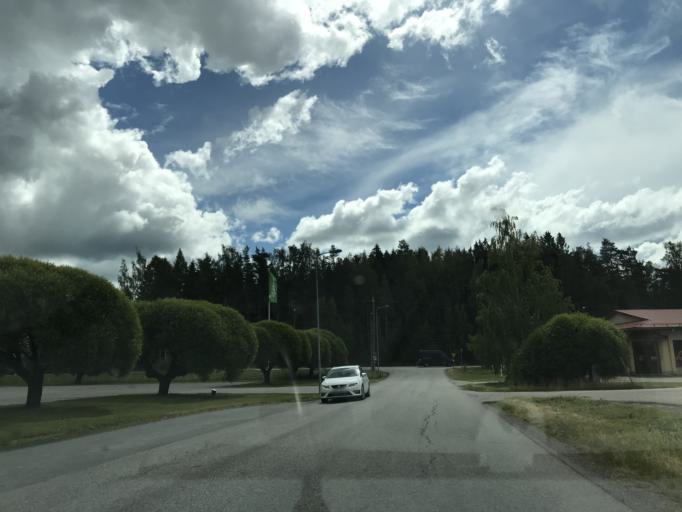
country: FI
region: Uusimaa
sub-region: Helsinki
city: Maentsaelae
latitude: 60.6238
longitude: 25.2884
